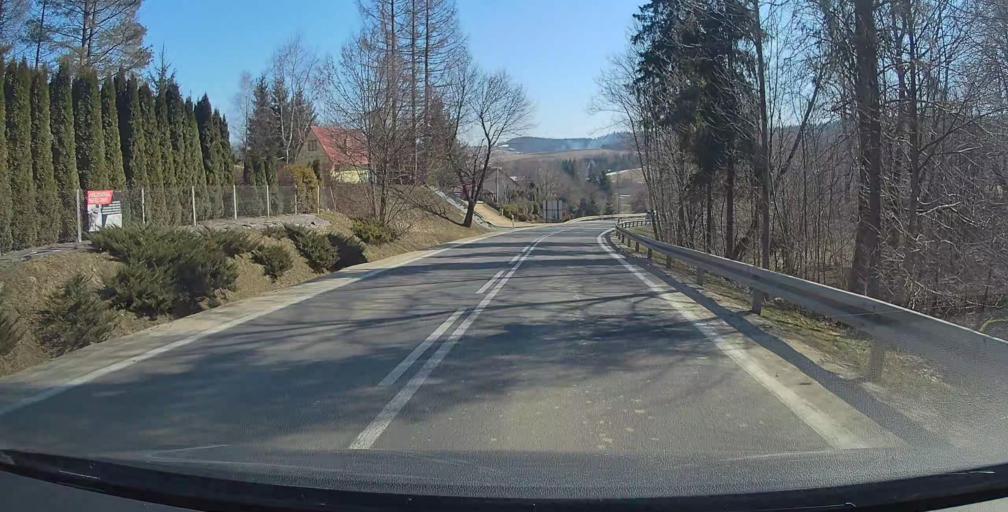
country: PL
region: Subcarpathian Voivodeship
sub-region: Powiat sanocki
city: Tyrawa Woloska
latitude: 49.6182
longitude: 22.4288
